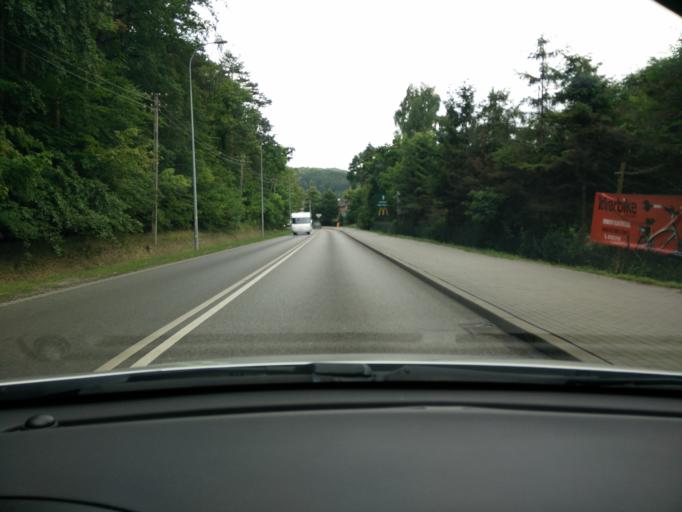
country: PL
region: Pomeranian Voivodeship
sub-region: Sopot
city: Sopot
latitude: 54.4135
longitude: 18.5472
